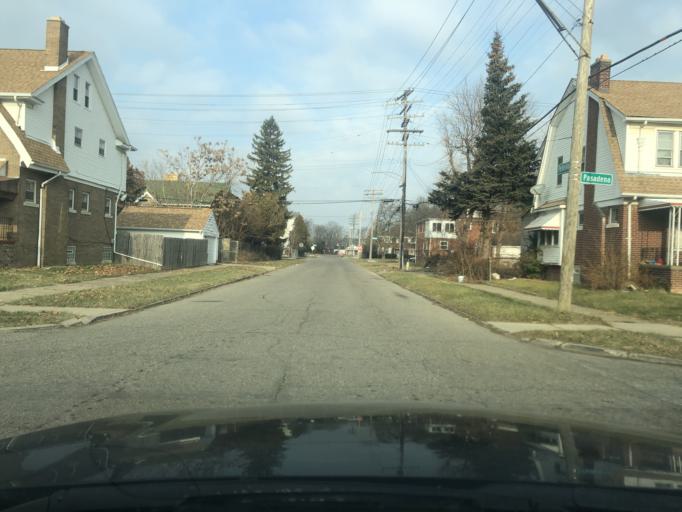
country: US
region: Michigan
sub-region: Wayne County
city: Highland Park
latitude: 42.3904
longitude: -83.1369
